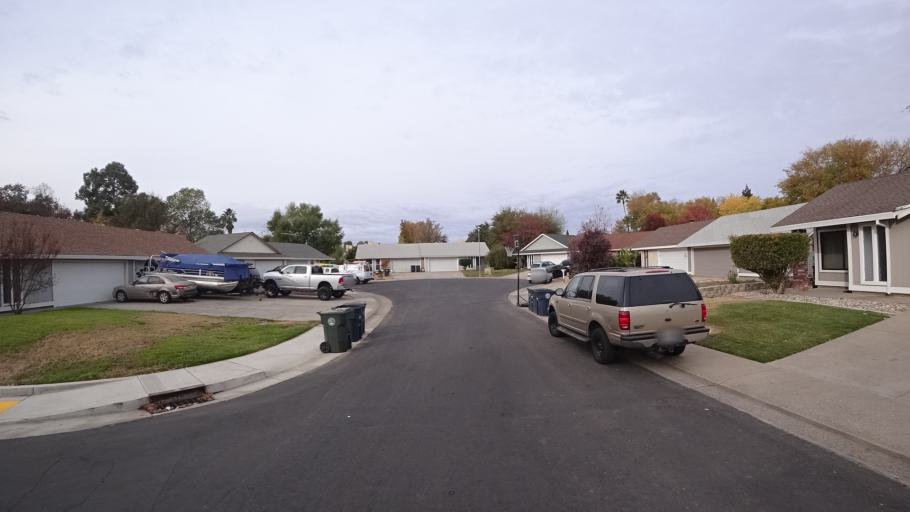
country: US
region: California
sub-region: Sacramento County
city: Citrus Heights
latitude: 38.7176
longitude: -121.2910
